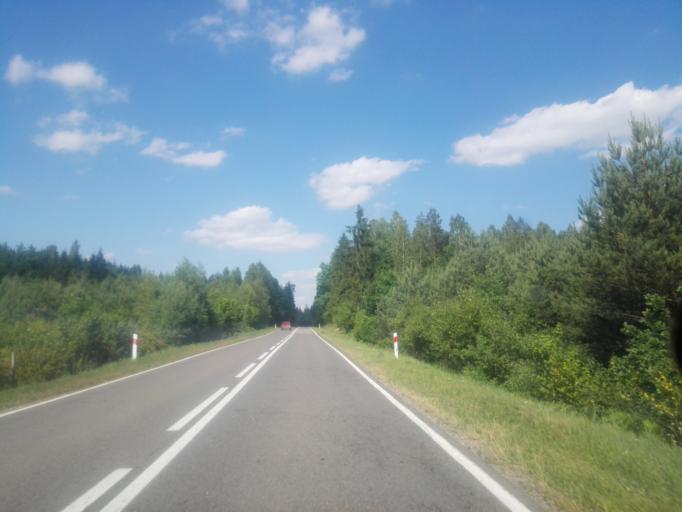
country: PL
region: Podlasie
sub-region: Powiat sejnenski
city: Sejny
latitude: 54.0053
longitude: 23.3207
